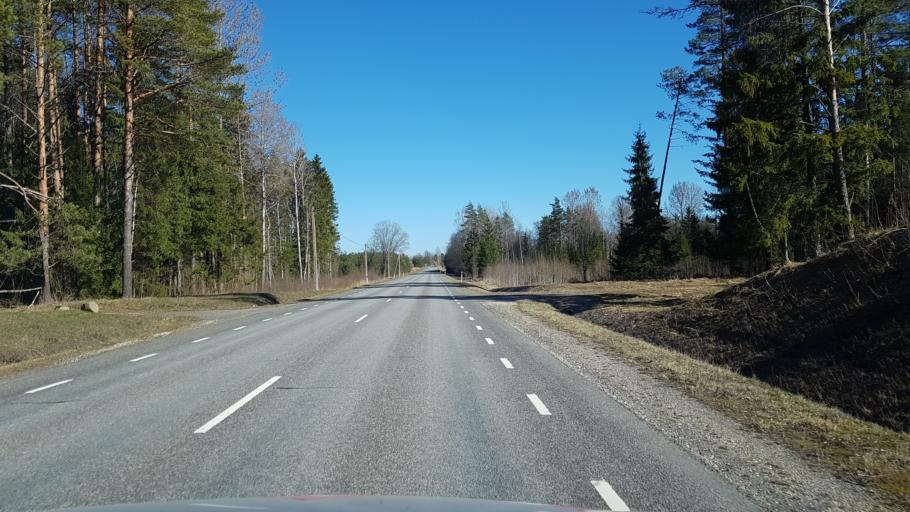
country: EE
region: Ida-Virumaa
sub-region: Aseri vald
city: Aseri
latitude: 59.3512
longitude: 26.7494
